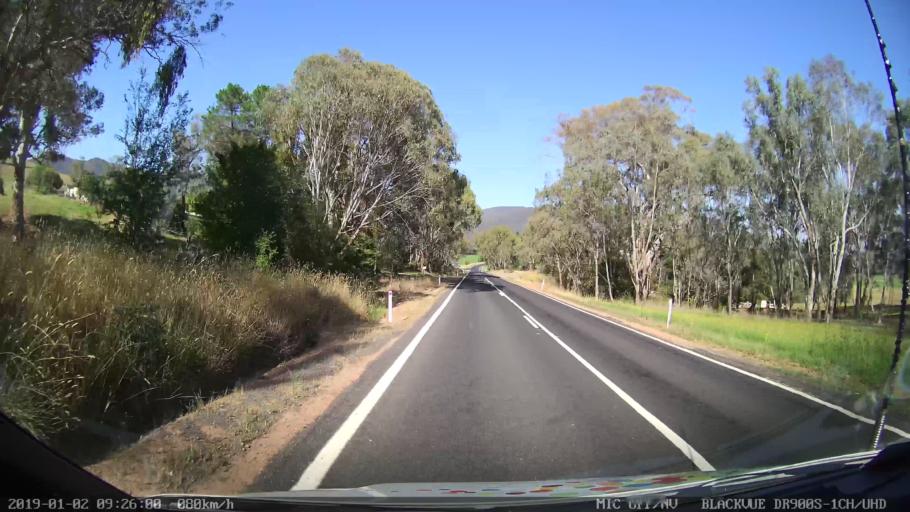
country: AU
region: New South Wales
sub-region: Tumut Shire
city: Tumut
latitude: -35.3647
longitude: 148.2786
